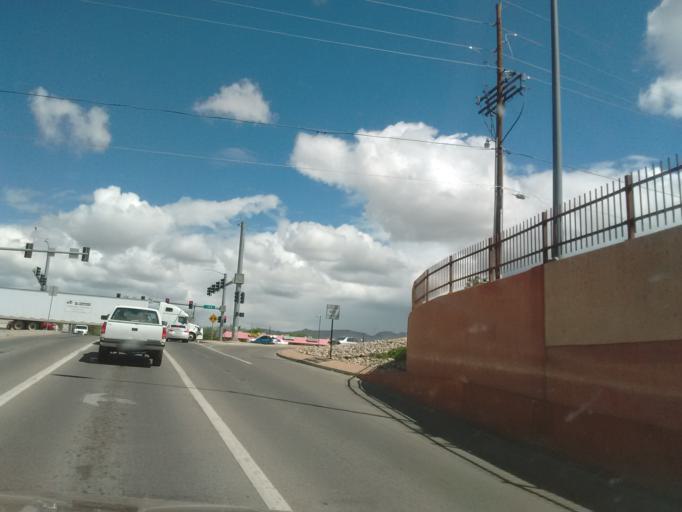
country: US
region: Colorado
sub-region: Mesa County
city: Fruitvale
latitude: 39.0772
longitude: -108.4965
